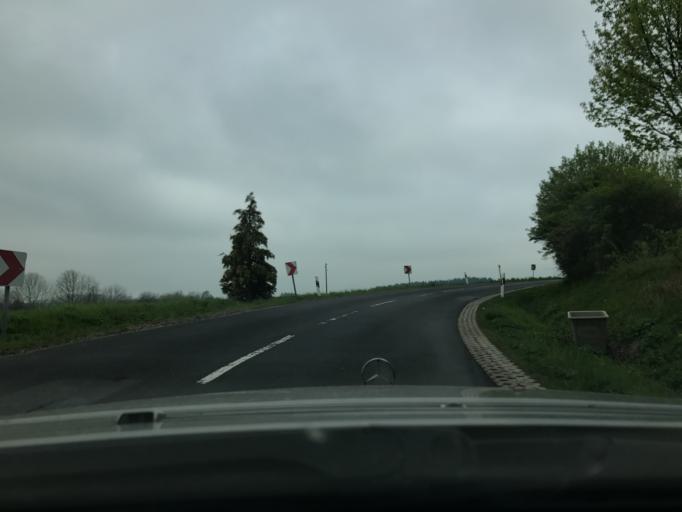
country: DE
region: Thuringia
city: Kefferhausen
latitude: 51.3173
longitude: 10.2800
